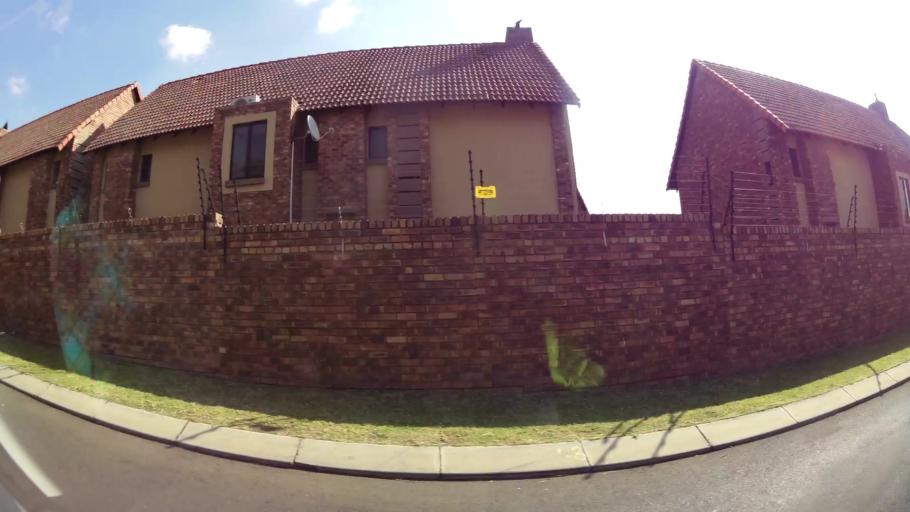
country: ZA
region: Gauteng
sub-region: City of Johannesburg Metropolitan Municipality
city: Modderfontein
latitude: -26.0886
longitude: 28.2632
